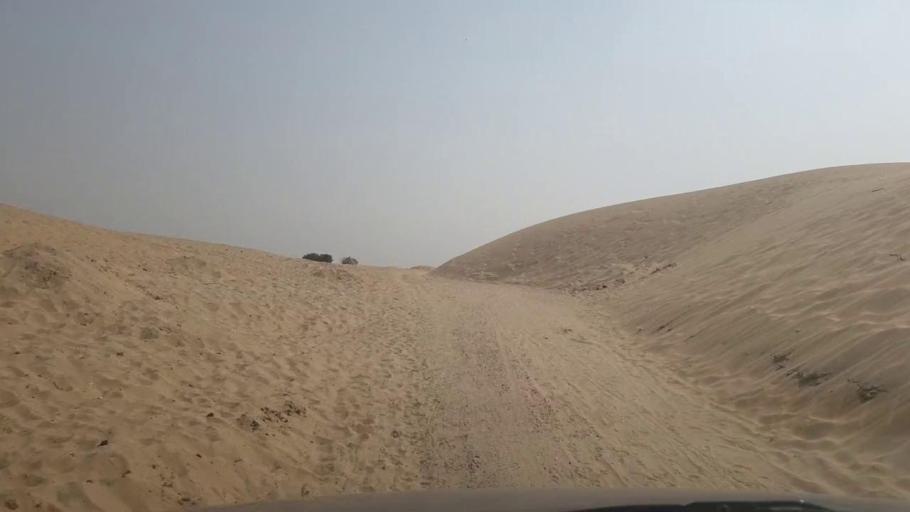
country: PK
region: Sindh
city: Chor
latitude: 25.5852
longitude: 70.0081
